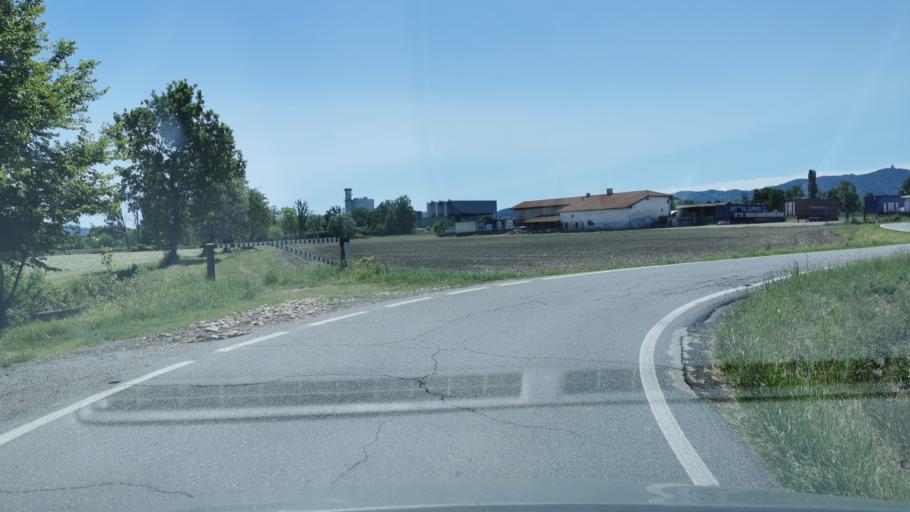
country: IT
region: Piedmont
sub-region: Provincia di Torino
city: Leini
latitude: 45.1680
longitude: 7.7427
